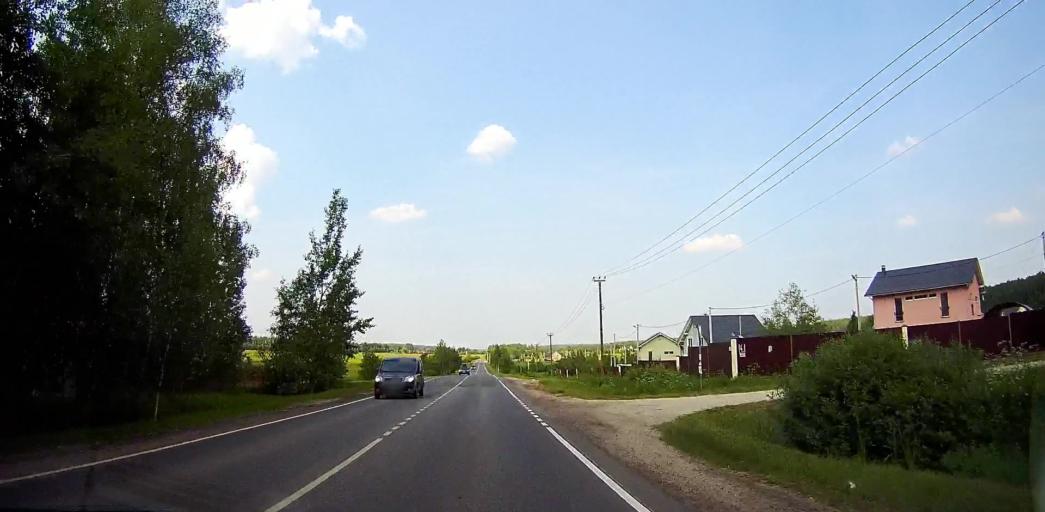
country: RU
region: Moskovskaya
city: Mikhnevo
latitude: 55.1716
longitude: 37.9635
